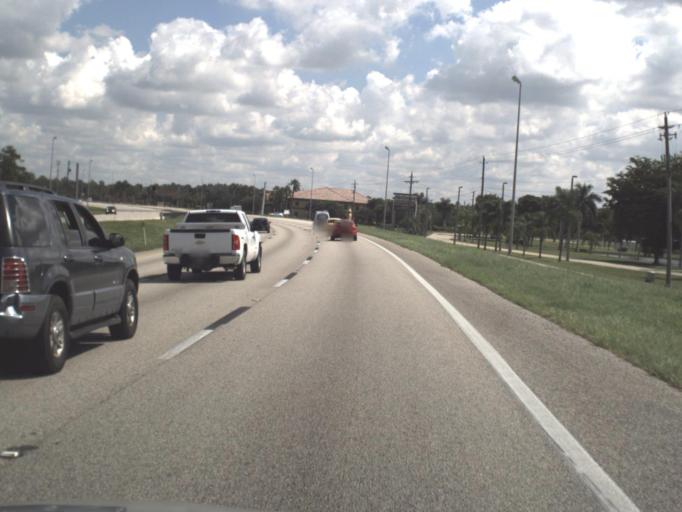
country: US
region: Florida
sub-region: Lee County
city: Fort Myers
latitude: 26.5975
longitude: -81.8382
